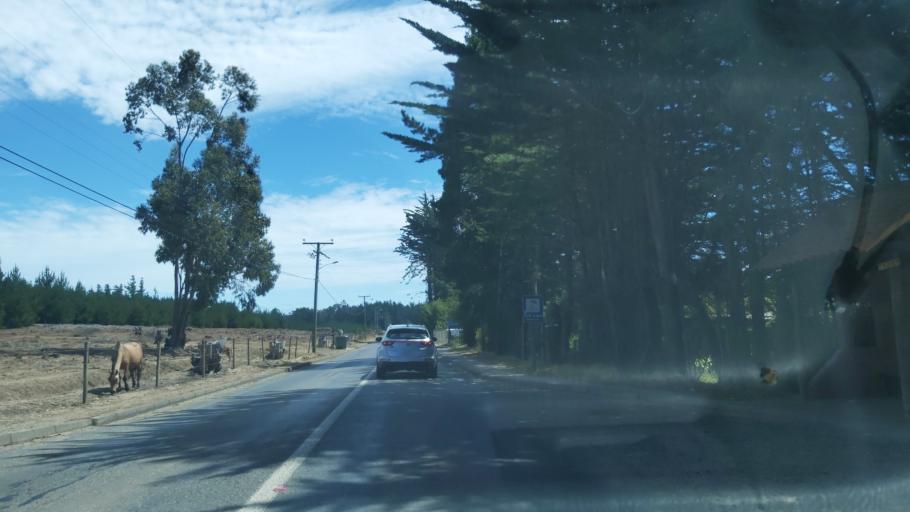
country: CL
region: Maule
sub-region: Provincia de Talca
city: Constitucion
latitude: -35.5091
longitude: -72.5226
